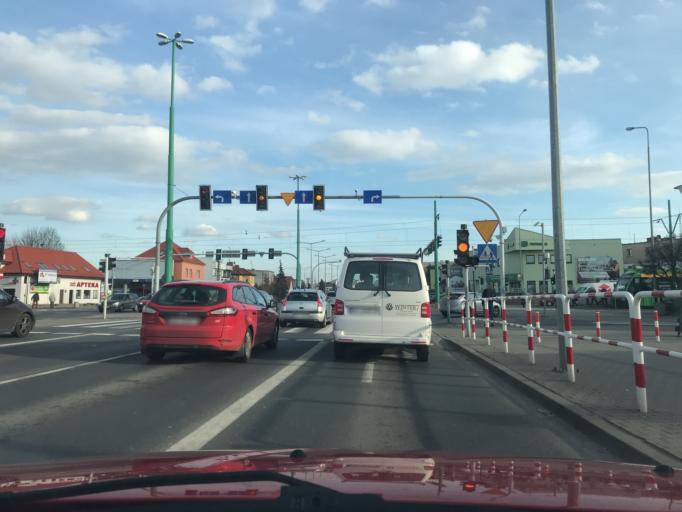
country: PL
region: Greater Poland Voivodeship
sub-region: Powiat poznanski
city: Lubon
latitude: 52.3959
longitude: 16.8621
